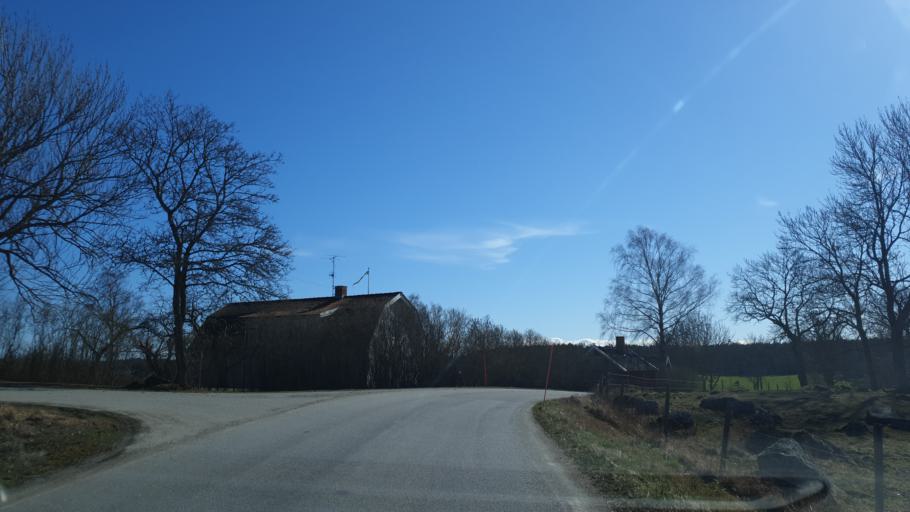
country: SE
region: Uppsala
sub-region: Enkopings Kommun
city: Dalby
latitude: 59.5577
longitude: 17.3147
